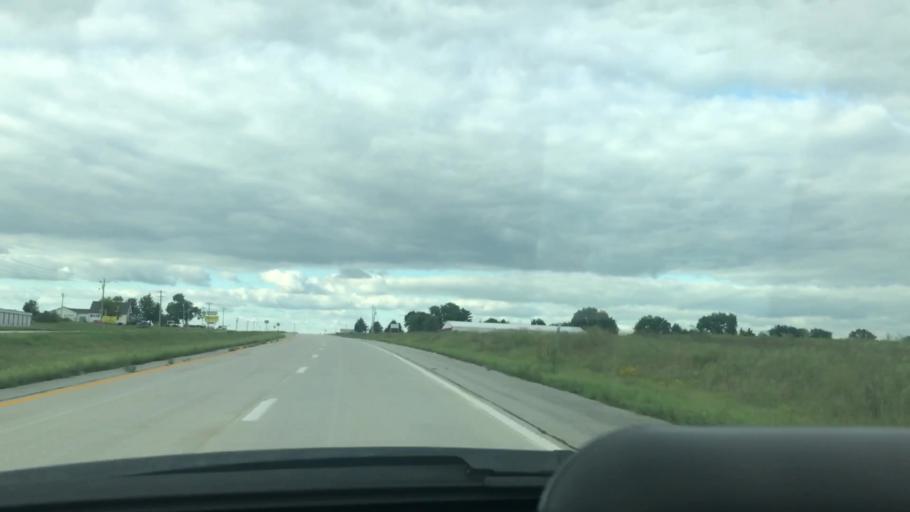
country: US
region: Missouri
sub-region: Benton County
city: Lincoln
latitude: 38.3374
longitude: -93.3407
